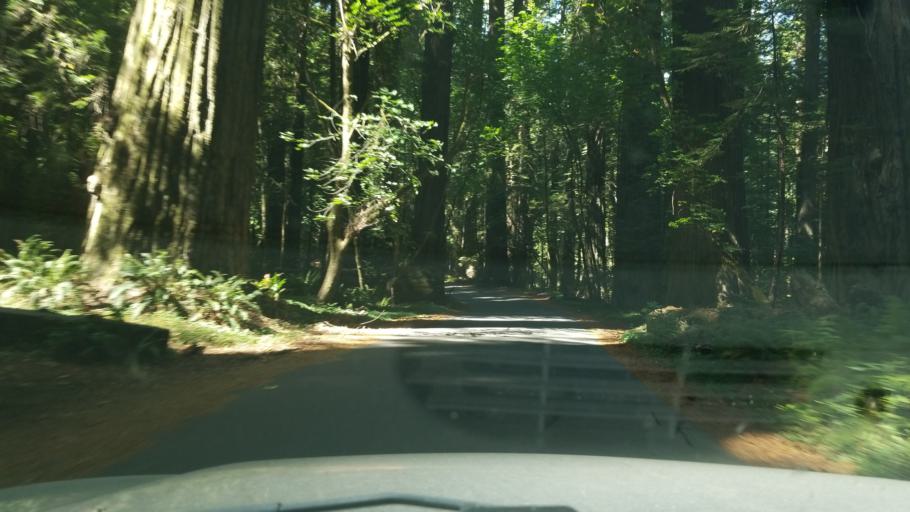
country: US
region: California
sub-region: Humboldt County
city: Rio Dell
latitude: 40.3516
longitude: -123.9218
